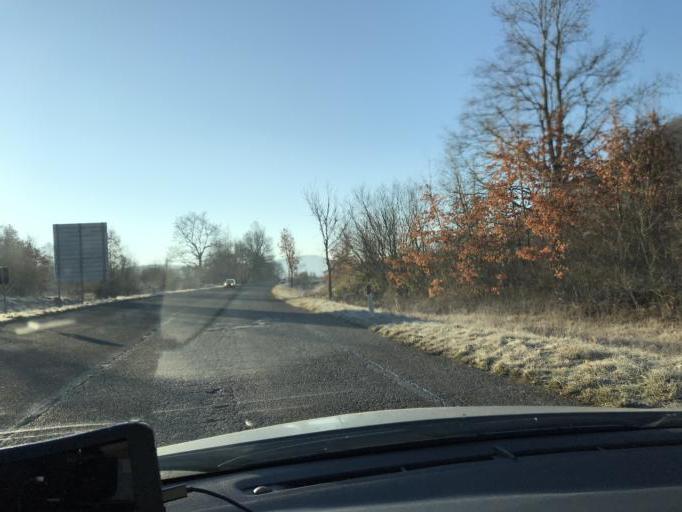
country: IT
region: Latium
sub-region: Provincia di Rieti
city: Borgorose
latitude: 42.2275
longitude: 13.1955
